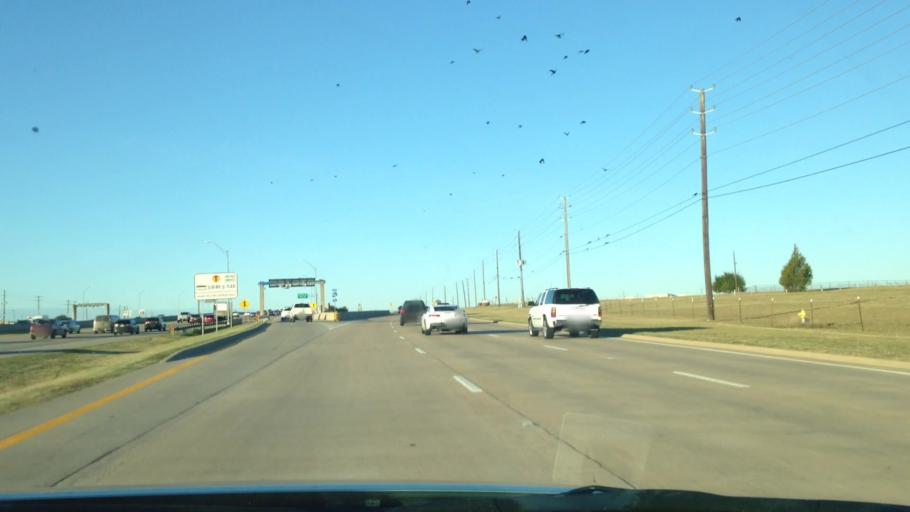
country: US
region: Texas
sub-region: Collin County
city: Frisco
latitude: 33.1153
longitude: -96.7615
